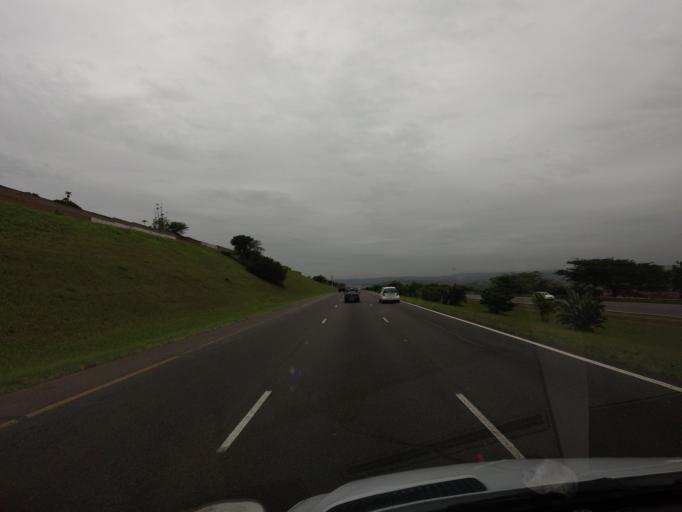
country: ZA
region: KwaZulu-Natal
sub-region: eThekwini Metropolitan Municipality
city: Durban
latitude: -29.7378
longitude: 31.0496
